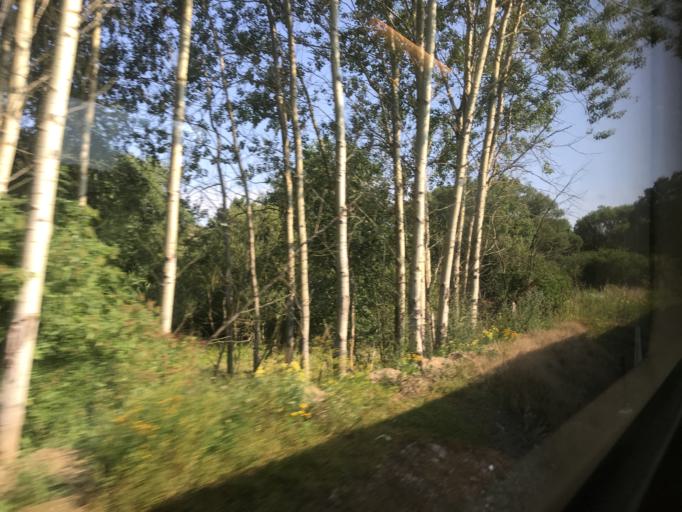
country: CZ
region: Central Bohemia
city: Votice
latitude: 49.6218
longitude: 14.5994
